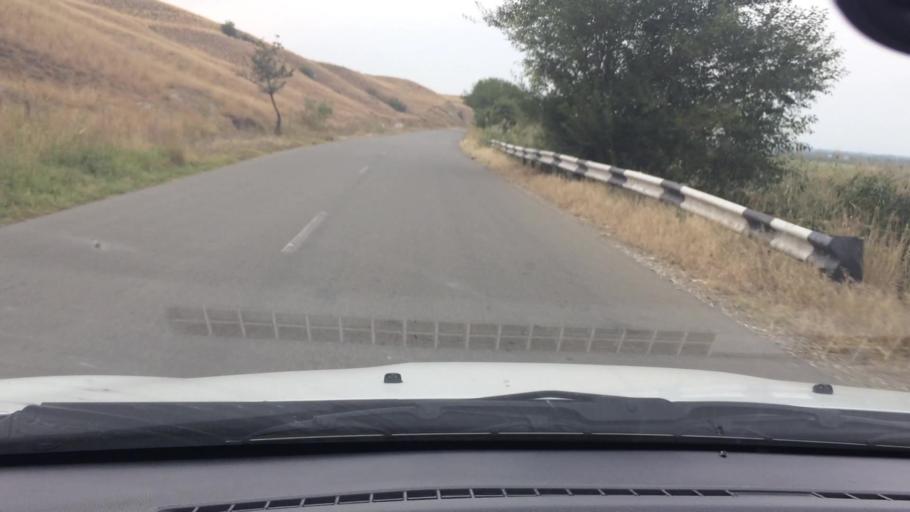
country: AM
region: Tavush
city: Berdavan
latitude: 41.3384
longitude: 45.0015
